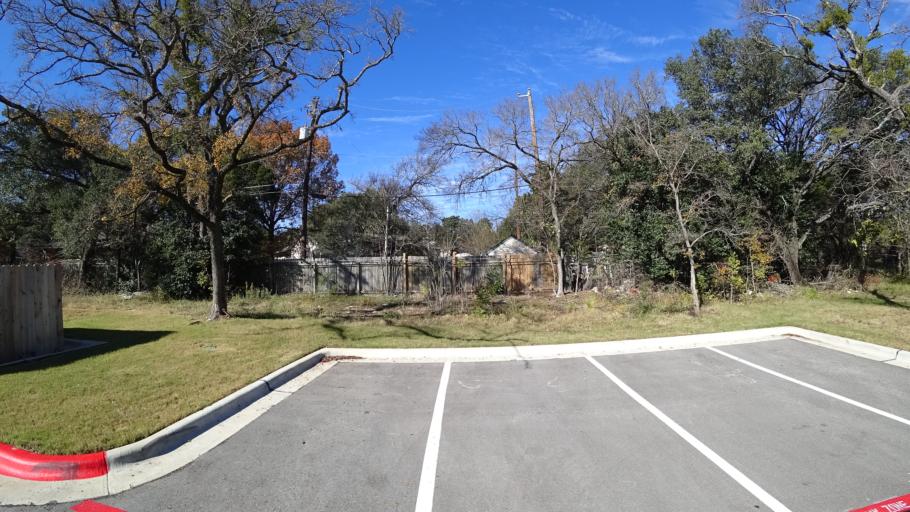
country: US
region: Texas
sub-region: Travis County
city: Wells Branch
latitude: 30.4266
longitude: -97.7054
